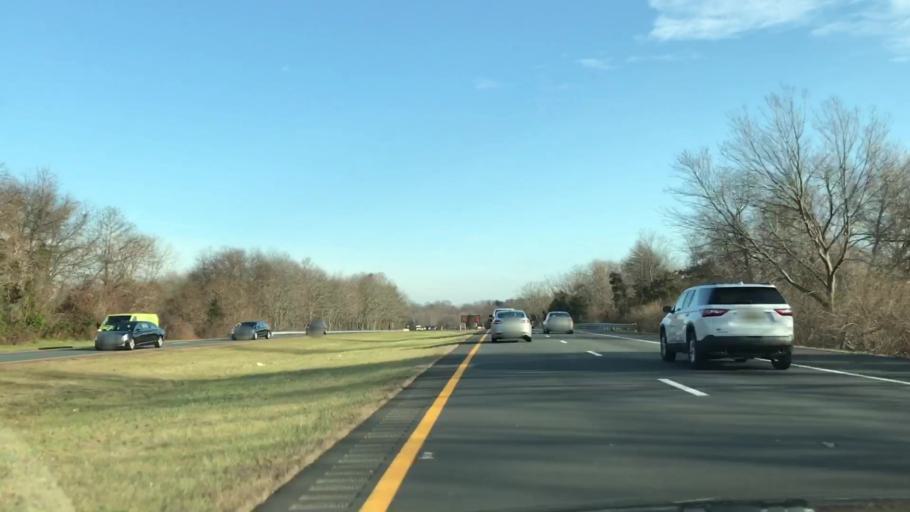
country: US
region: New Jersey
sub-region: Monmouth County
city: Shrewsbury
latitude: 40.1743
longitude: -74.4961
